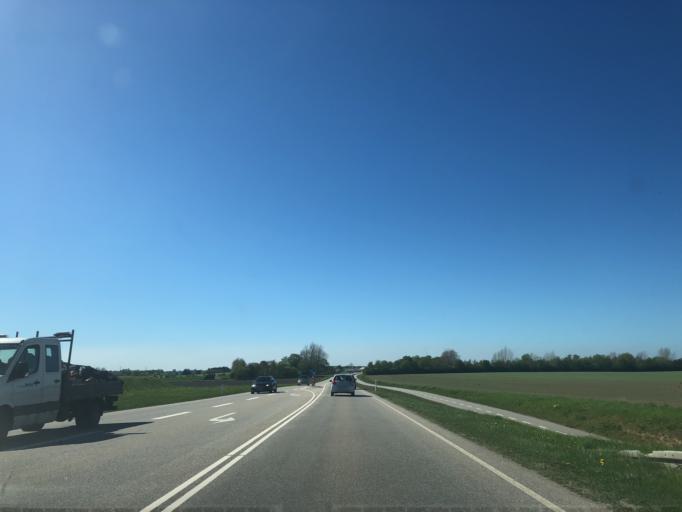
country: DK
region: Zealand
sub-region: Stevns Kommune
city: Store Heddinge
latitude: 55.3531
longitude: 12.3258
